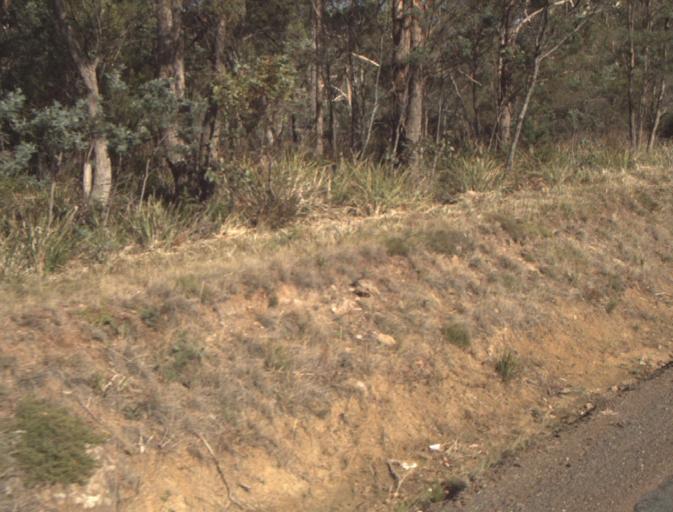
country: AU
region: Tasmania
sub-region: Launceston
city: Mayfield
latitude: -41.3408
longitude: 147.1433
